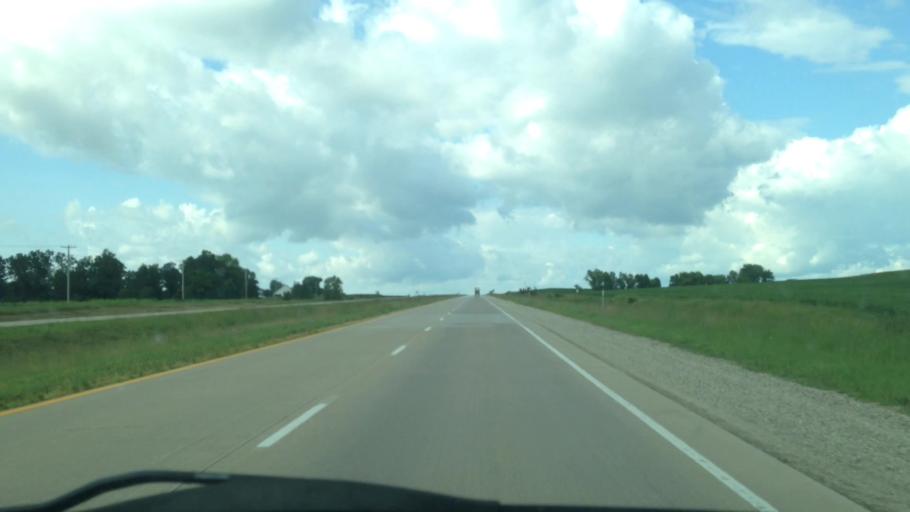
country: US
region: Illinois
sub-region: Hancock County
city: Nauvoo
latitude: 40.5830
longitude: -91.5646
